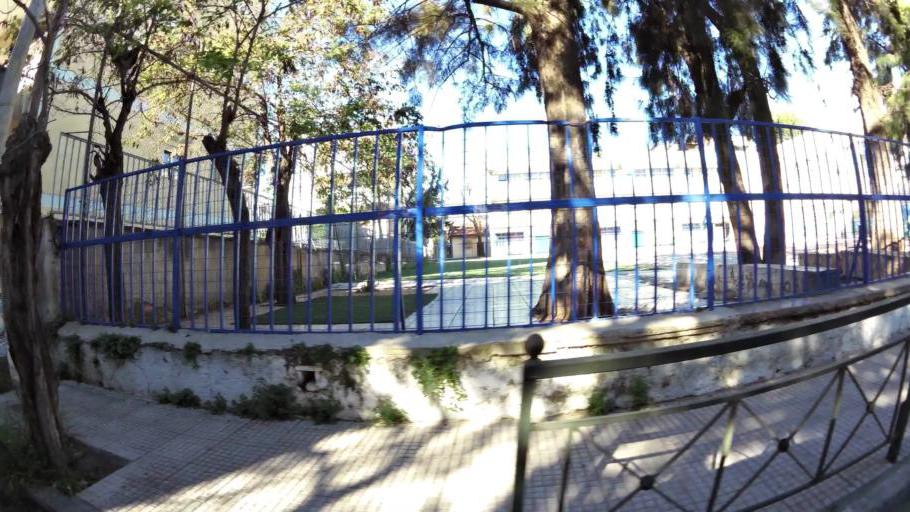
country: GR
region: Attica
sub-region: Nomarchia Athinas
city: Khalandrion
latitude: 38.0188
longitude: 23.8002
